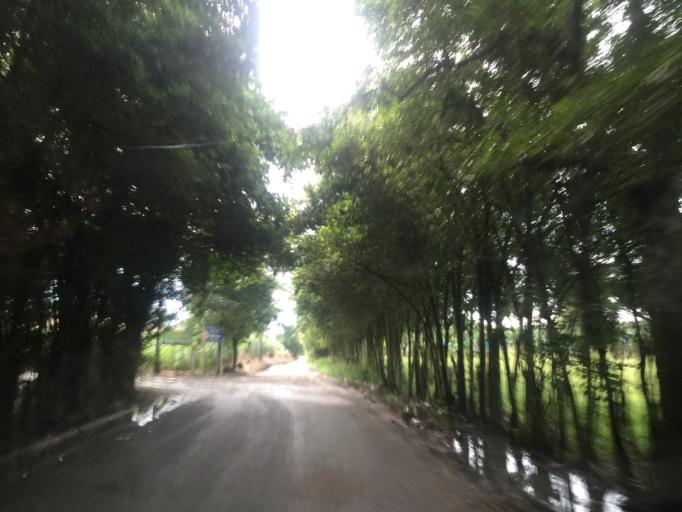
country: CO
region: Quindio
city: La Tebaida
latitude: 4.4679
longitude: -75.8306
